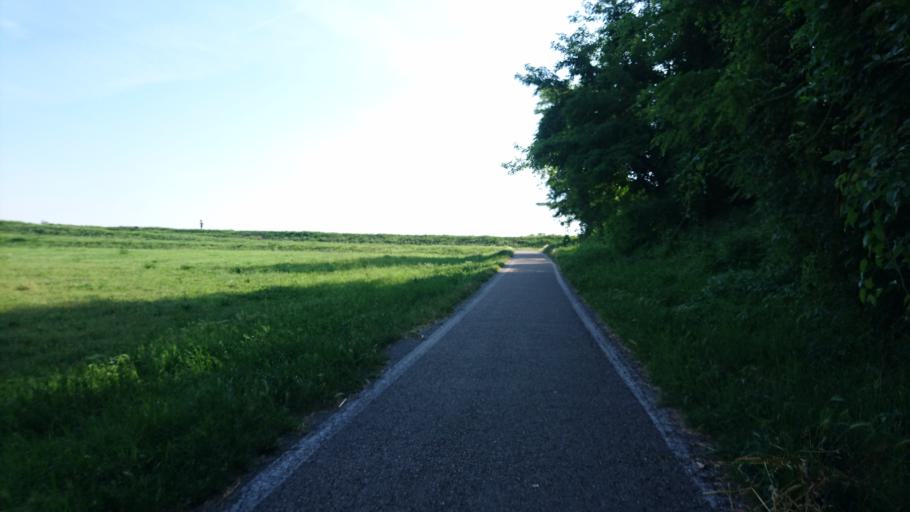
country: IT
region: Veneto
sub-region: Provincia di Verona
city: Boschi Sant'Anna
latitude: 45.1900
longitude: 11.3148
